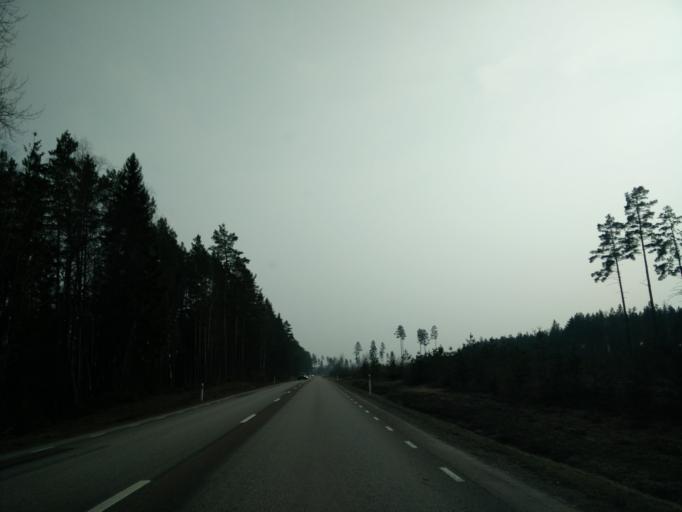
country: SE
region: Vaermland
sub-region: Forshaga Kommun
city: Forshaga
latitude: 59.5050
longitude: 13.4355
